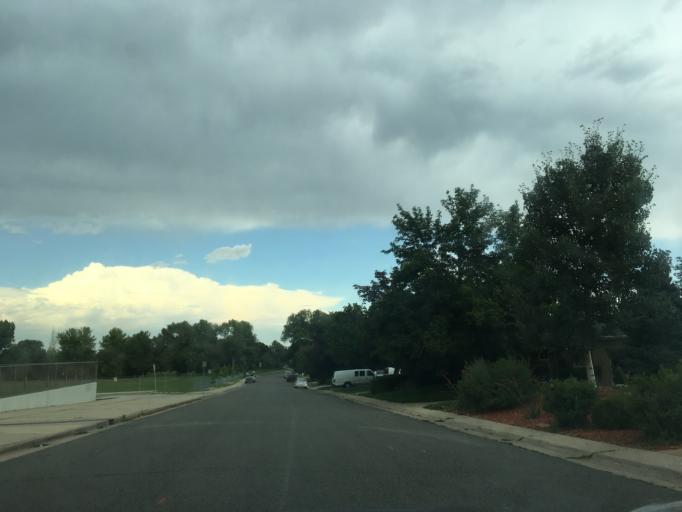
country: US
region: Colorado
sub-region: Arapahoe County
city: Sheridan
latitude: 39.6758
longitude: -105.0387
